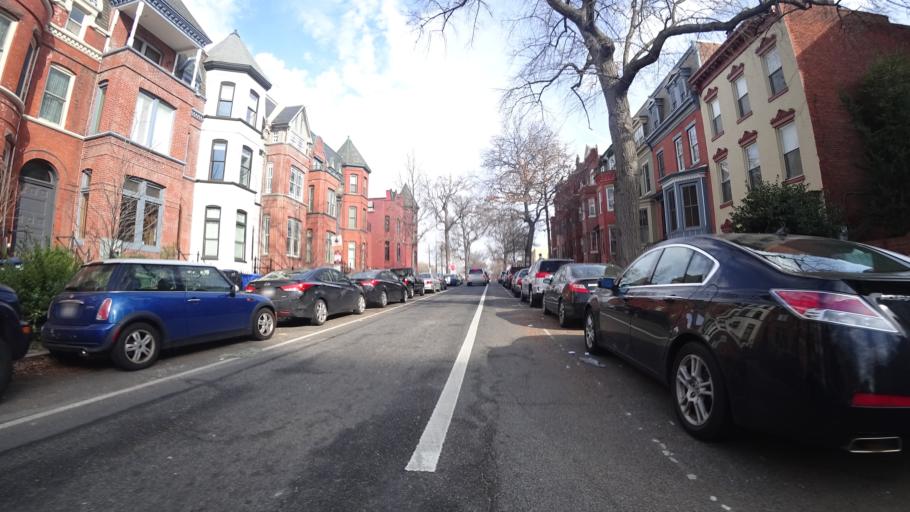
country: US
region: Washington, D.C.
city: Washington, D.C.
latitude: 38.9049
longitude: -77.0189
